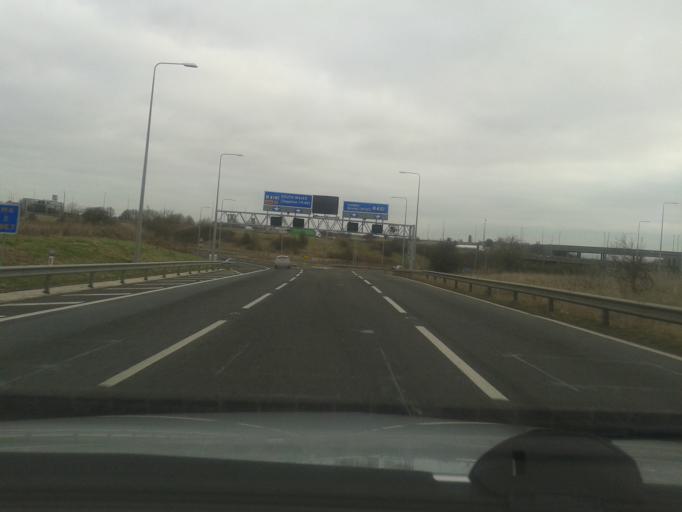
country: GB
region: England
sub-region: South Gloucestershire
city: Almondsbury
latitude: 51.5509
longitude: -2.5576
